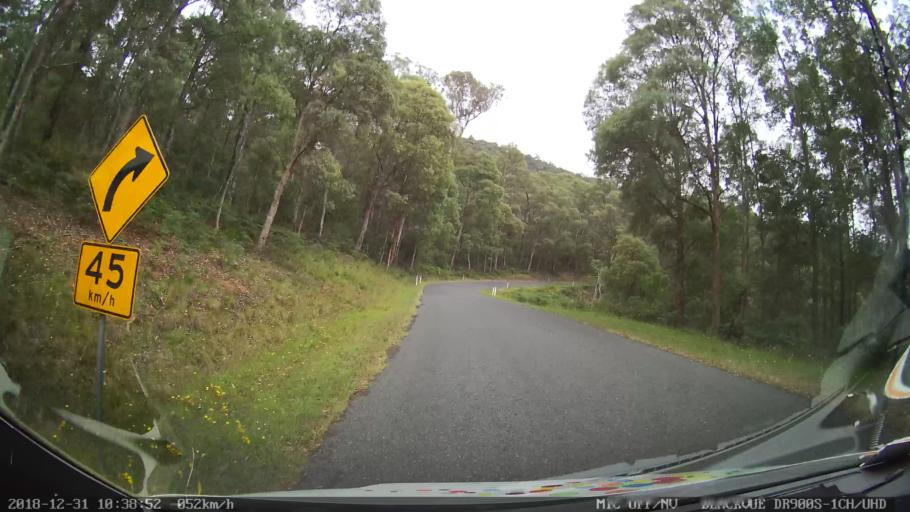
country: AU
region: New South Wales
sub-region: Snowy River
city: Jindabyne
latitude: -36.4038
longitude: 148.1774
